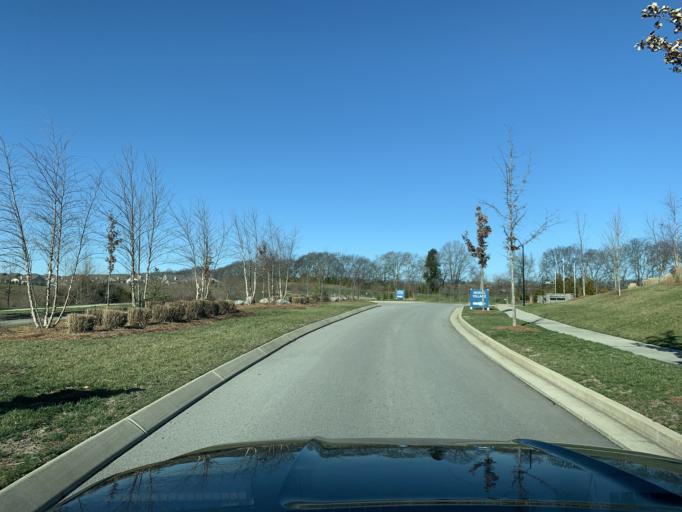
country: US
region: Tennessee
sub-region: Maury County
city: Spring Hill
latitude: 35.7254
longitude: -86.9266
